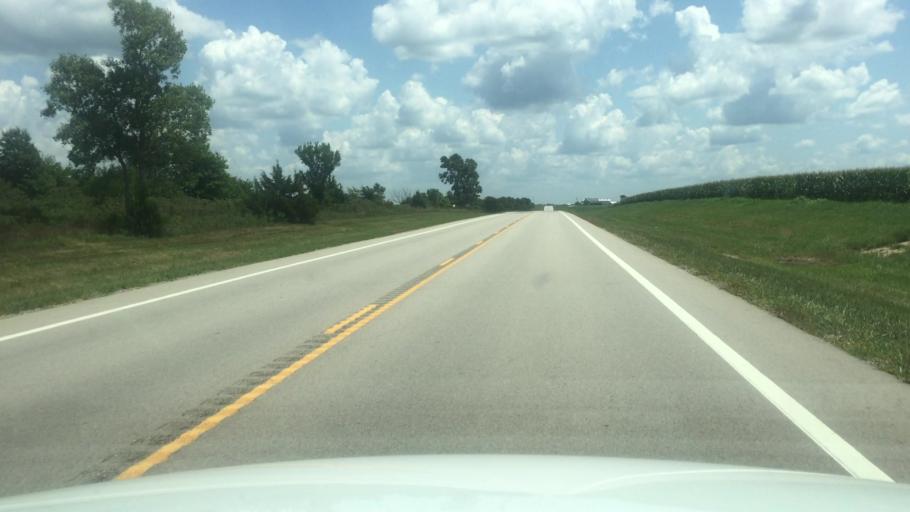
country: US
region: Kansas
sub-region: Brown County
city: Horton
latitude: 39.6571
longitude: -95.3742
